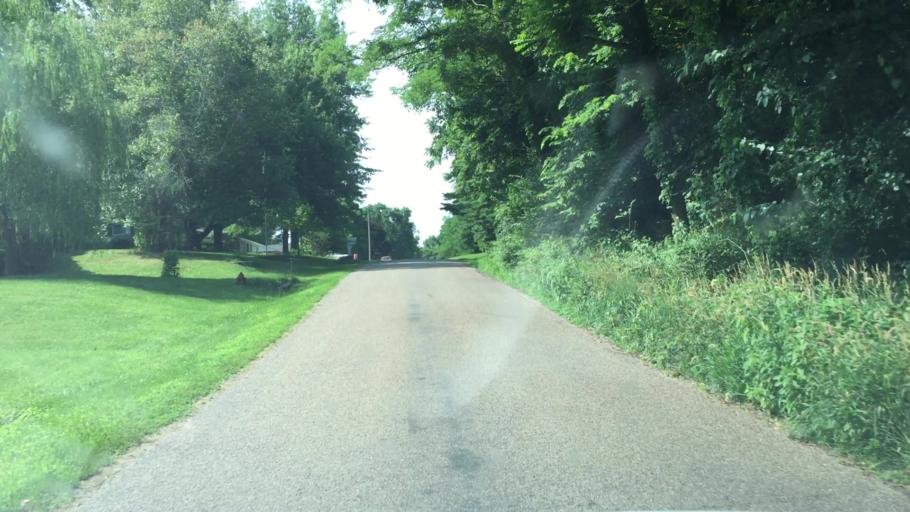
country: US
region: Illinois
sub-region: Hancock County
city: Nauvoo
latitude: 40.5460
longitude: -91.3754
